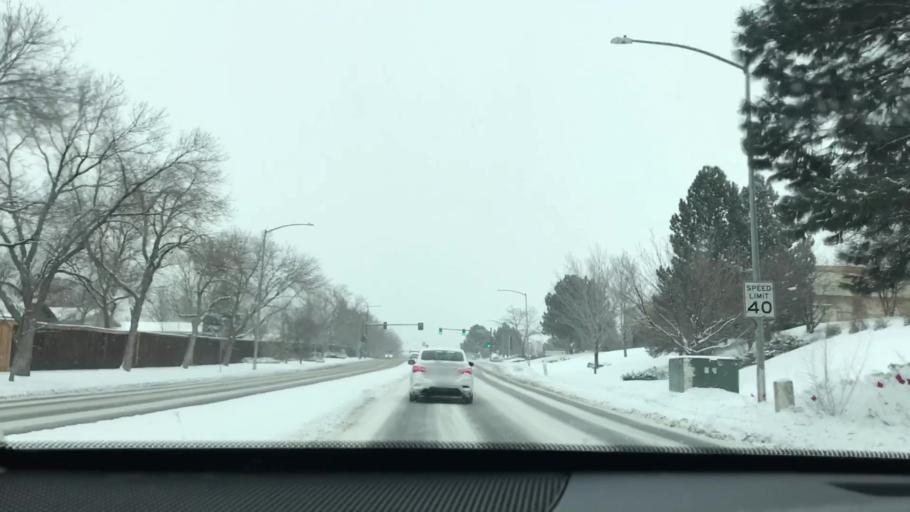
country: US
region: Colorado
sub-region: Adams County
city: Westminster
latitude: 39.8637
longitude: -105.0677
